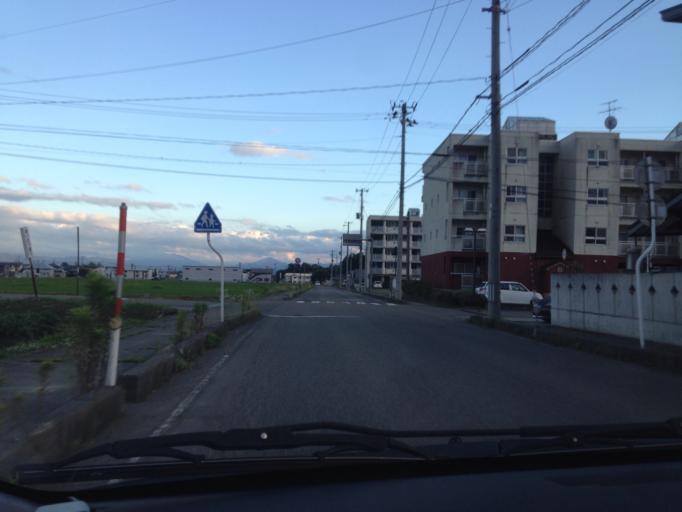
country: JP
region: Fukushima
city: Kitakata
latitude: 37.6708
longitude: 139.8653
